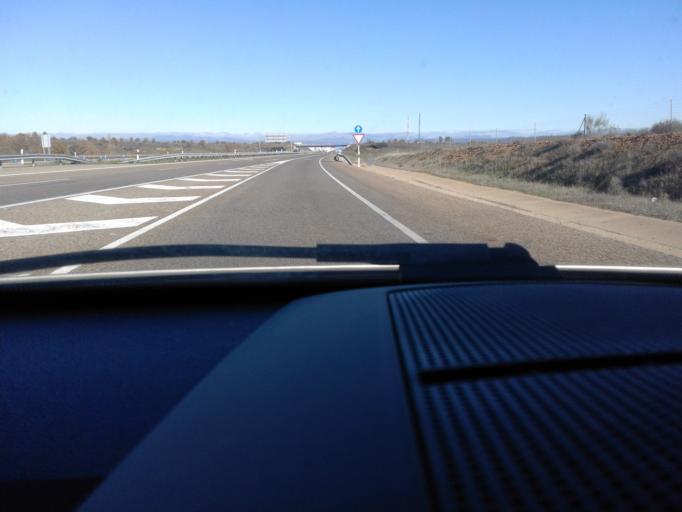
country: ES
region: Castille and Leon
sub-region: Provincia de Leon
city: Onzonilla
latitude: 42.5092
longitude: -5.5967
